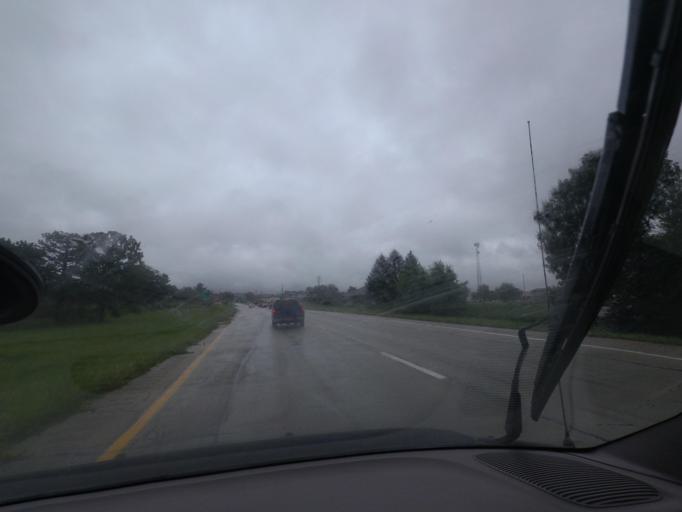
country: US
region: Illinois
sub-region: Champaign County
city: Champaign
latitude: 40.1166
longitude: -88.2835
